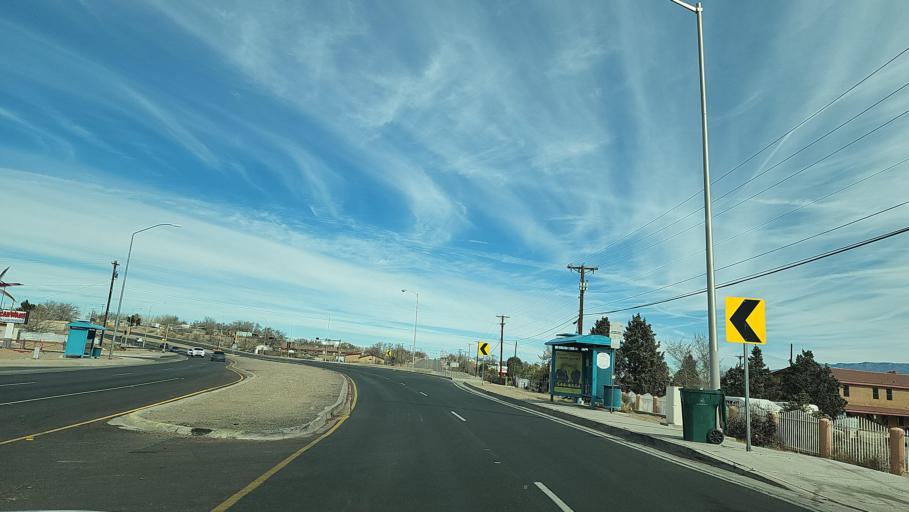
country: US
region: New Mexico
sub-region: Bernalillo County
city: South Valley
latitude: 35.0552
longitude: -106.7058
